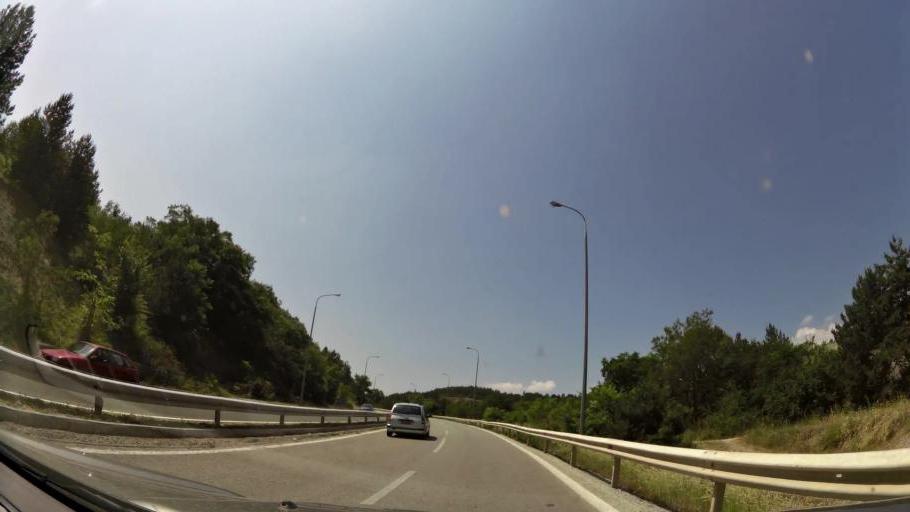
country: GR
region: West Macedonia
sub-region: Nomos Kozanis
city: Kozani
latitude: 40.3148
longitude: 21.7838
